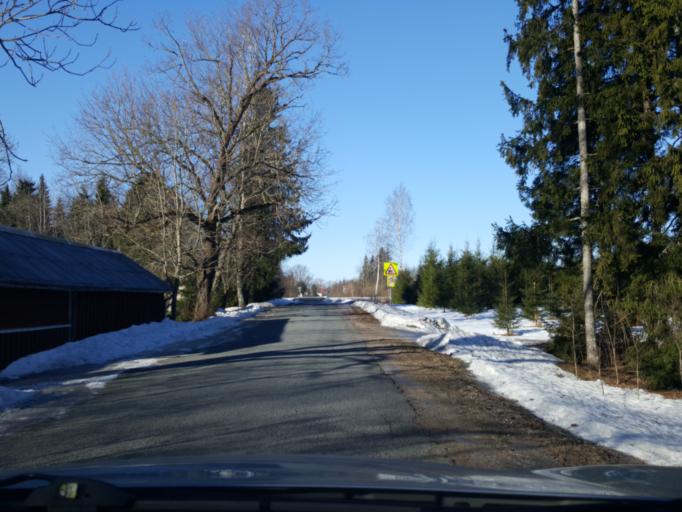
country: EE
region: Viljandimaa
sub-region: Suure-Jaani vald
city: Suure-Jaani
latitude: 58.5366
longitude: 25.5482
